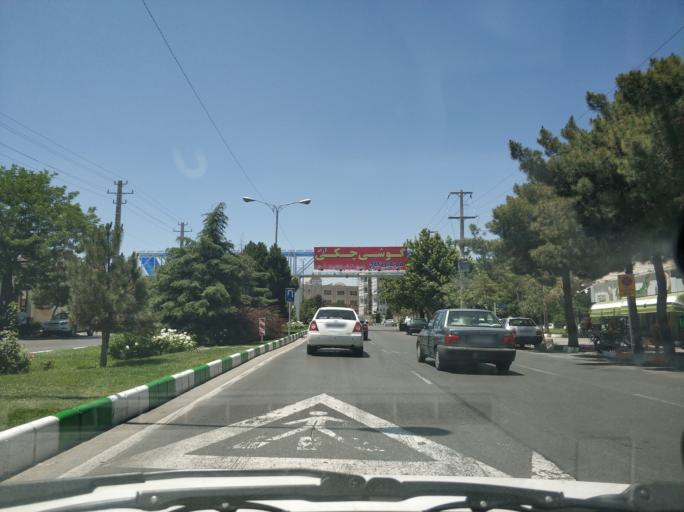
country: IR
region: Razavi Khorasan
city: Mashhad
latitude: 36.3134
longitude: 59.4914
